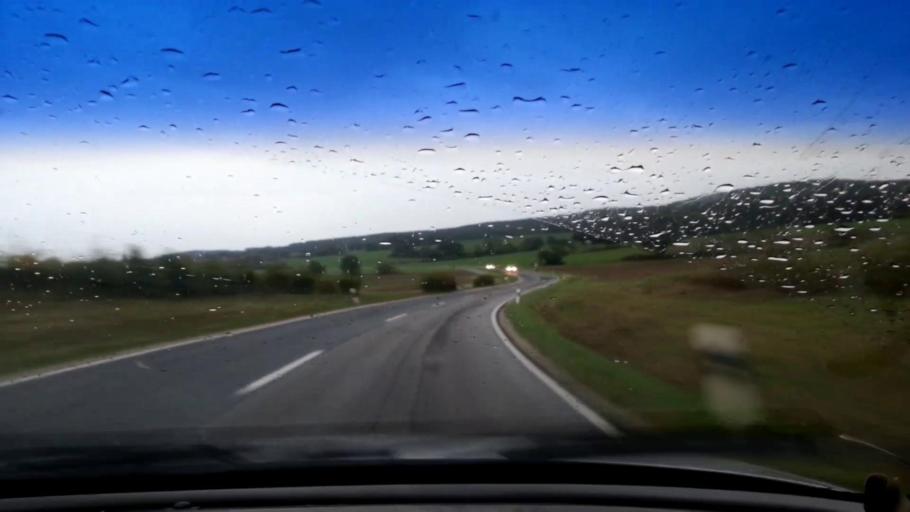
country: DE
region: Bavaria
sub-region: Upper Franconia
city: Burgebrach
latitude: 49.8482
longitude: 10.7162
